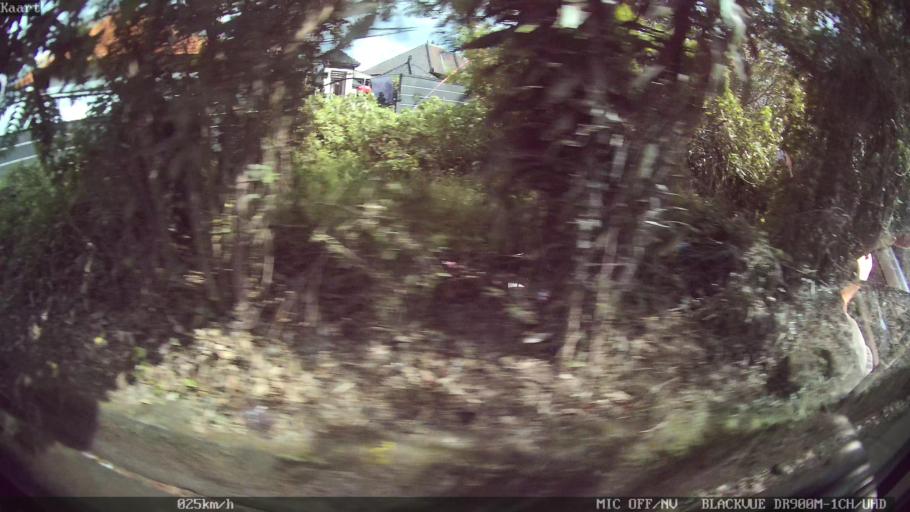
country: ID
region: Bali
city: Banjar Batur
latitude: -8.6065
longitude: 115.2049
